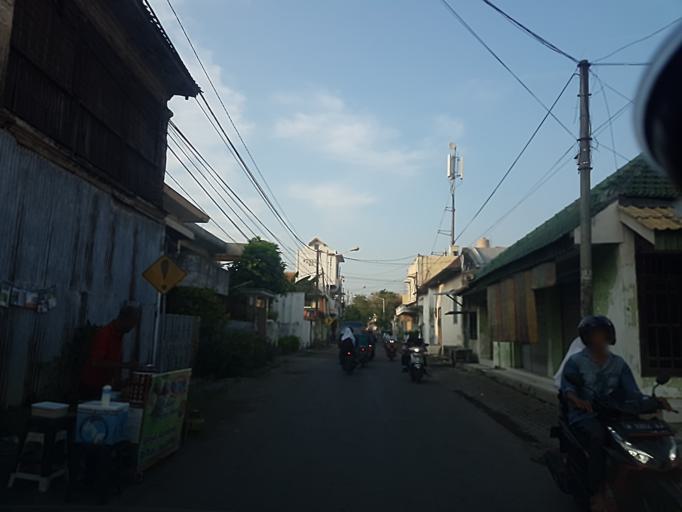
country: ID
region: East Java
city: Gresik
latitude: -7.1615
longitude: 112.6580
